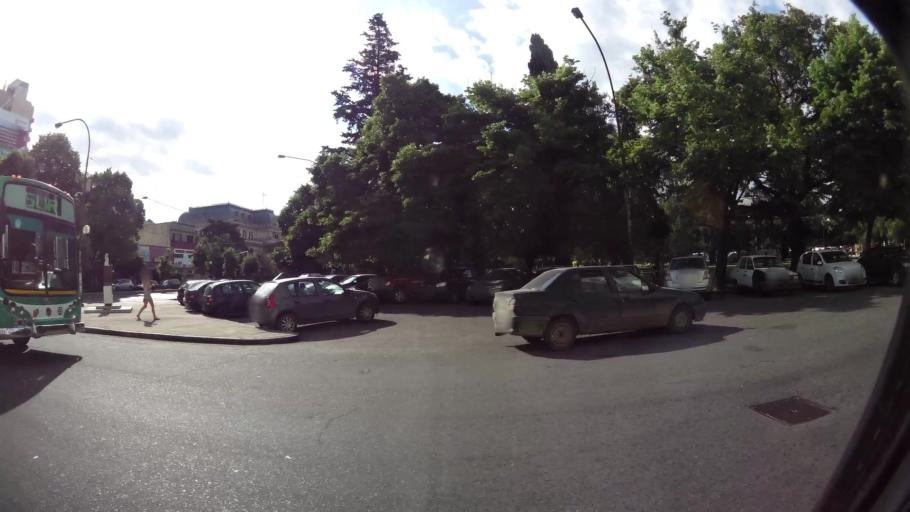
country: AR
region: Buenos Aires
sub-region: Partido de La Plata
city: La Plata
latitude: -34.9166
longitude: -57.9469
